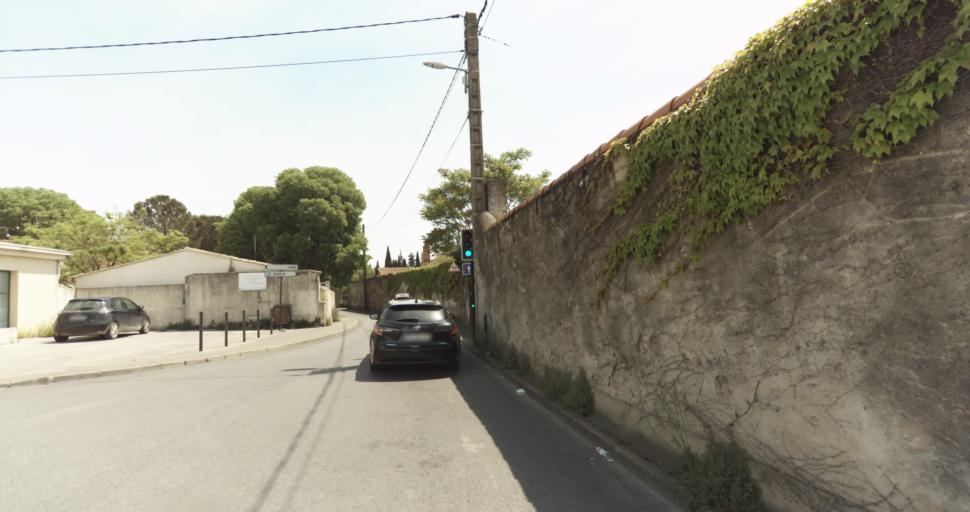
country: FR
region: Languedoc-Roussillon
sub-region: Departement du Gard
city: Nimes
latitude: 43.8469
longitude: 4.3743
